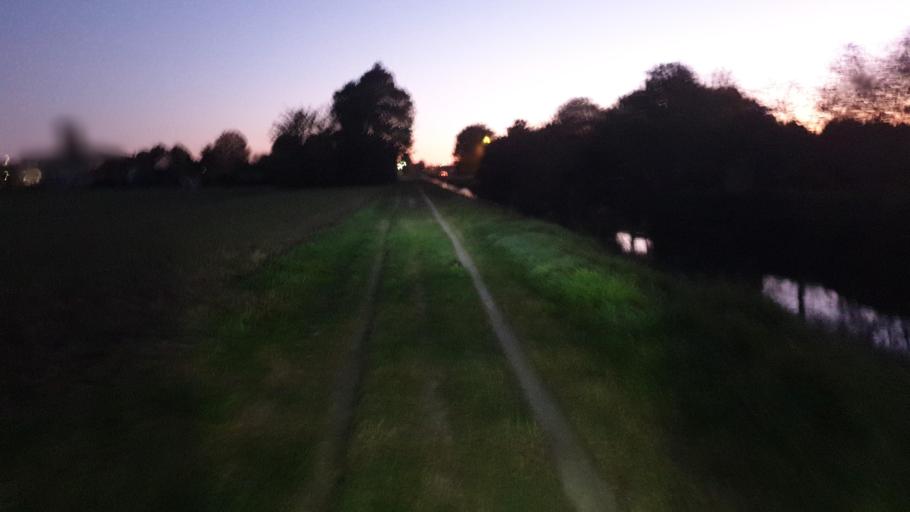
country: IT
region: Veneto
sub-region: Provincia di Venezia
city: Stra
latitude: 45.4210
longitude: 12.0097
